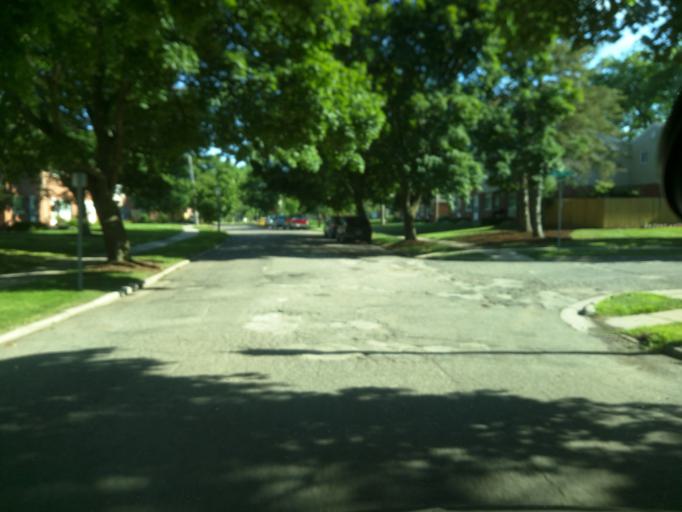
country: US
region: Michigan
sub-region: Ingham County
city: Lansing
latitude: 42.6936
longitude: -84.5841
